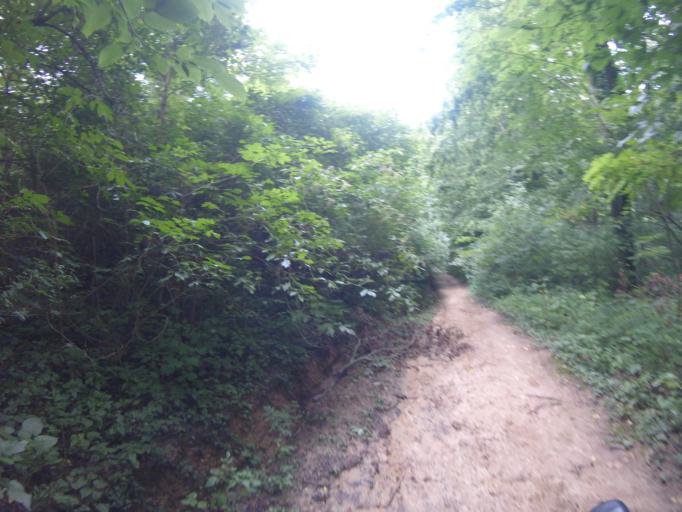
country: HU
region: Zala
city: Nagykanizsa
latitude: 46.5596
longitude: 17.0349
